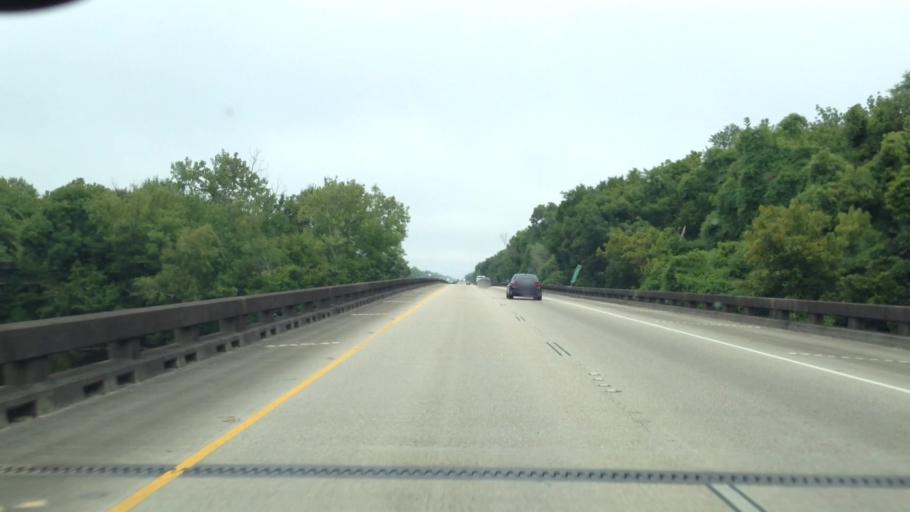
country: US
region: Louisiana
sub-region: Saint John the Baptist Parish
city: Montegut
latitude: 30.1079
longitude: -90.5078
